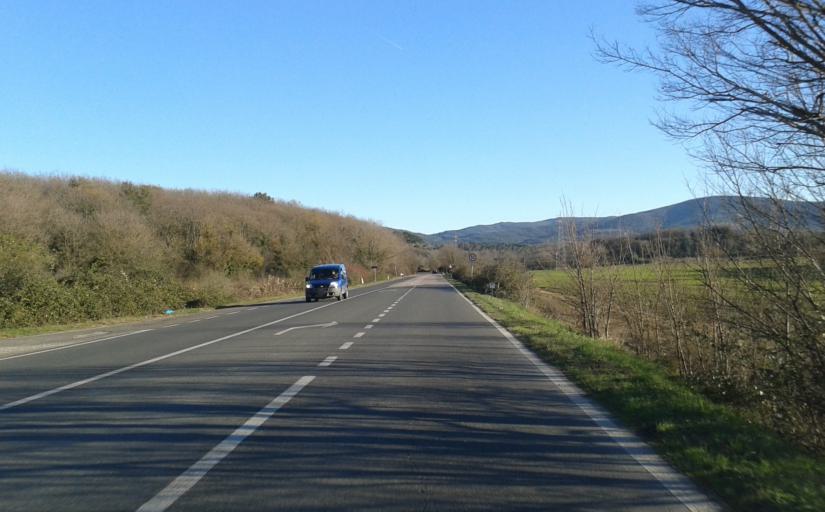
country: IT
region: Tuscany
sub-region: Provincia di Livorno
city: Livorno
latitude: 43.5706
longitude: 10.3546
